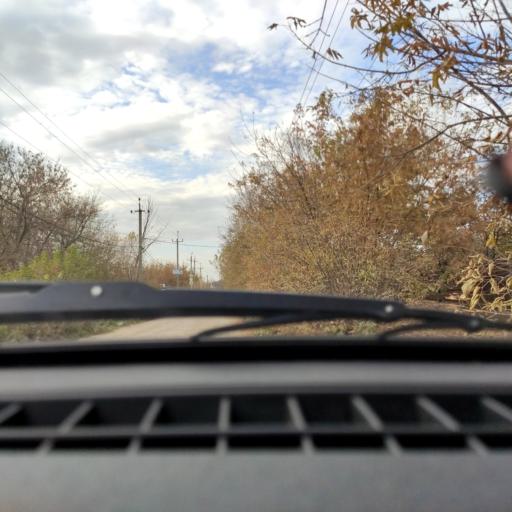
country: RU
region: Bashkortostan
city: Ufa
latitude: 54.7708
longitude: 55.9359
